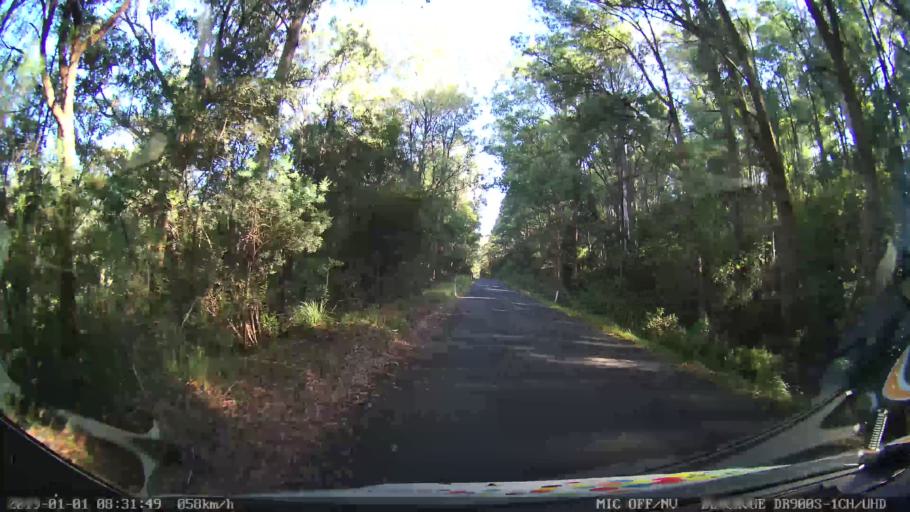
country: AU
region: New South Wales
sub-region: Snowy River
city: Jindabyne
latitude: -36.3672
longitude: 148.2055
